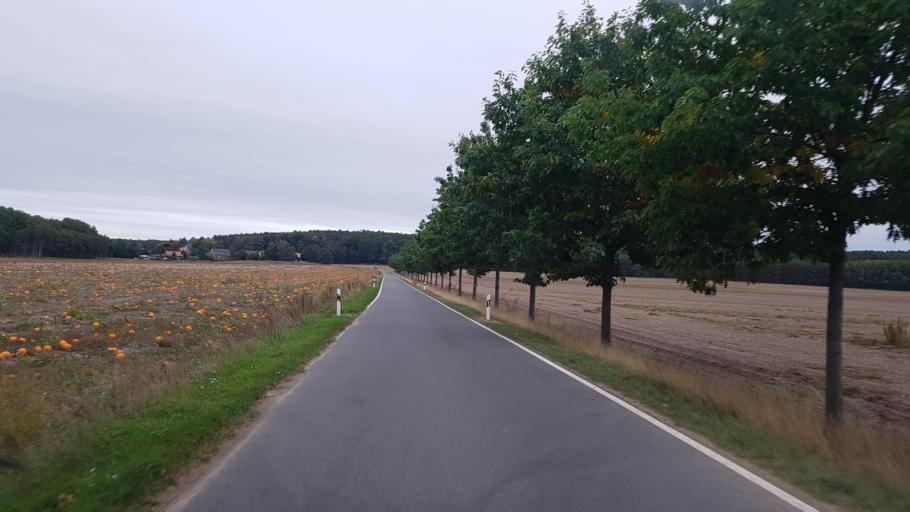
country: DE
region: Brandenburg
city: Drahnsdorf
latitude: 51.9492
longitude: 13.5451
